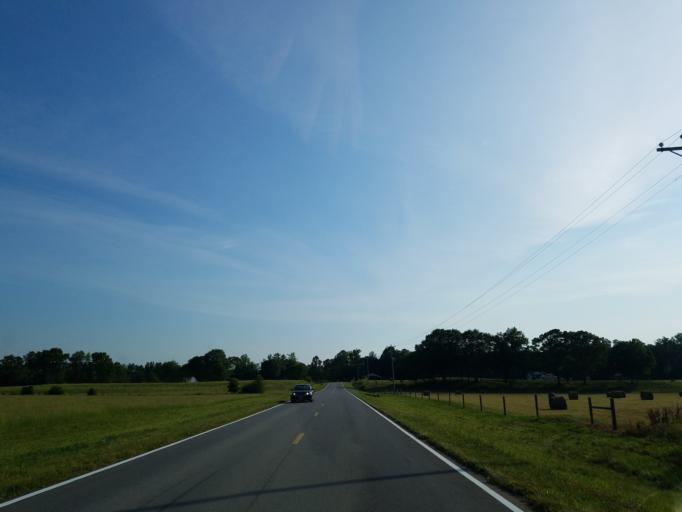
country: US
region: Georgia
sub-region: Chattooga County
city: Trion
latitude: 34.4834
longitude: -85.2574
